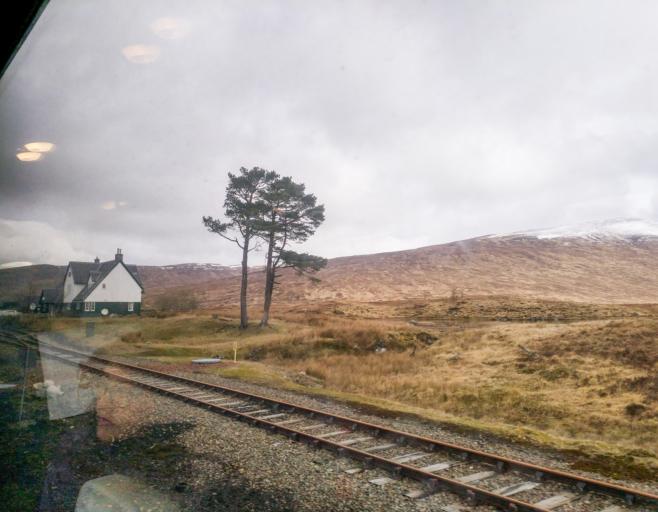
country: GB
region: Scotland
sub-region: Highland
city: Spean Bridge
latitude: 56.7596
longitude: -4.6897
